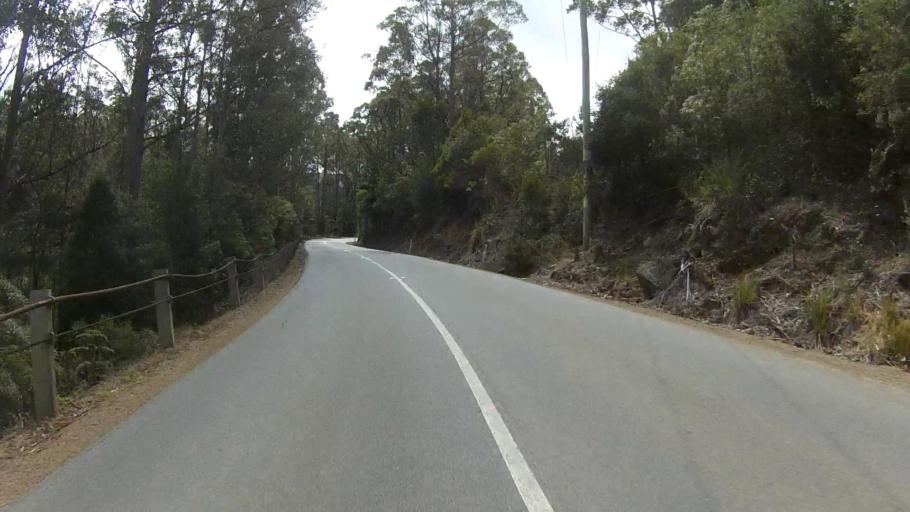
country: AU
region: Tasmania
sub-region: Kingborough
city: Kettering
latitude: -43.1252
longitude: 147.1832
